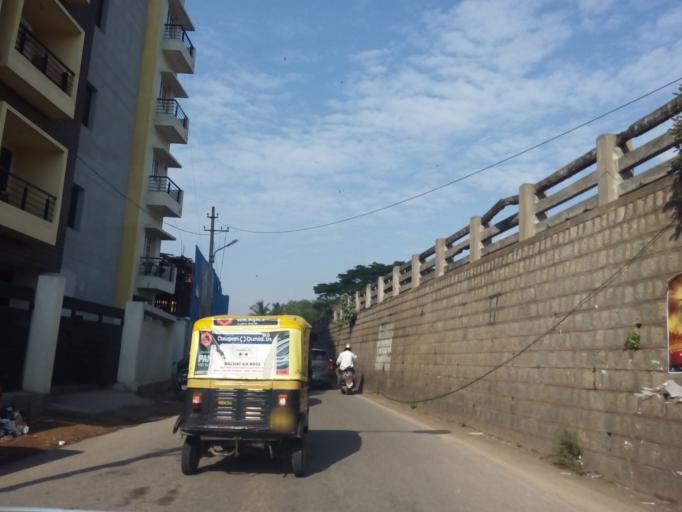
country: IN
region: Karnataka
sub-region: Bangalore Urban
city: Bangalore
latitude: 12.9940
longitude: 77.6060
